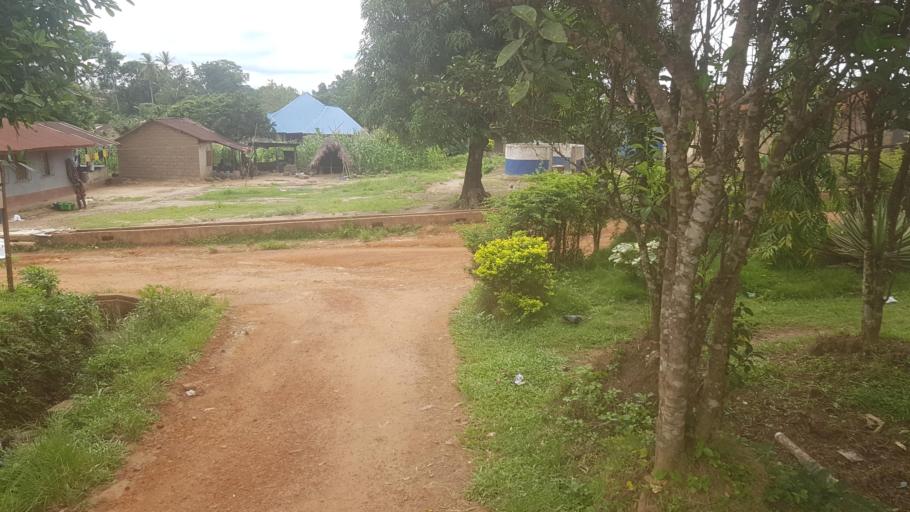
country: SL
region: Southern Province
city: Mogbwemo
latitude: 7.6102
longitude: -12.1789
